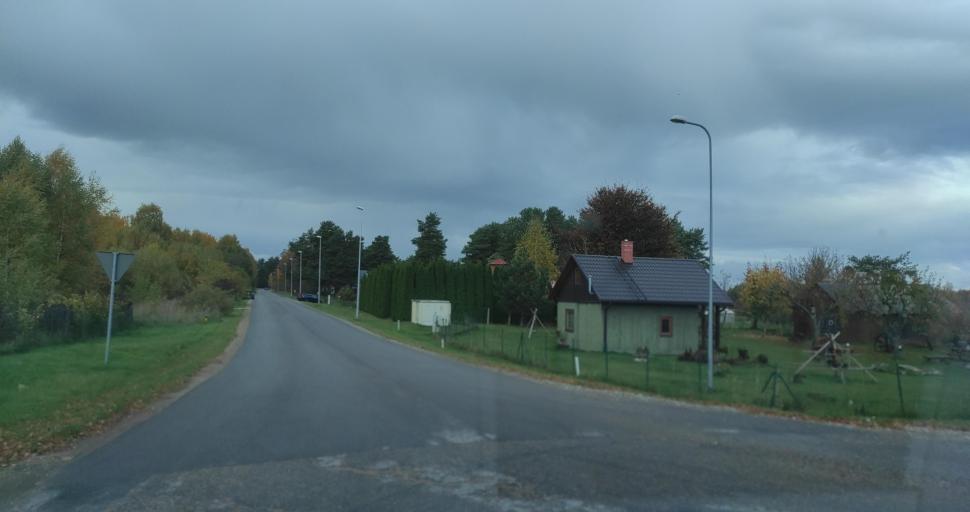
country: LV
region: Skrunda
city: Skrunda
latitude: 56.6819
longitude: 22.0158
